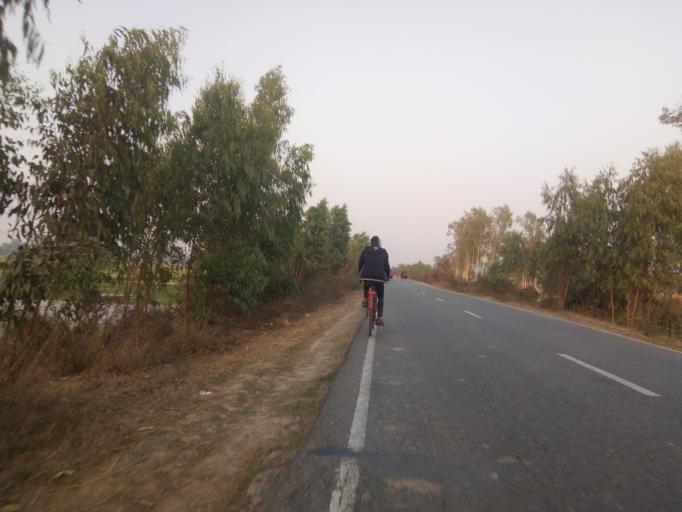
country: BD
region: Rajshahi
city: Bogra
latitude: 24.5850
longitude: 89.2290
